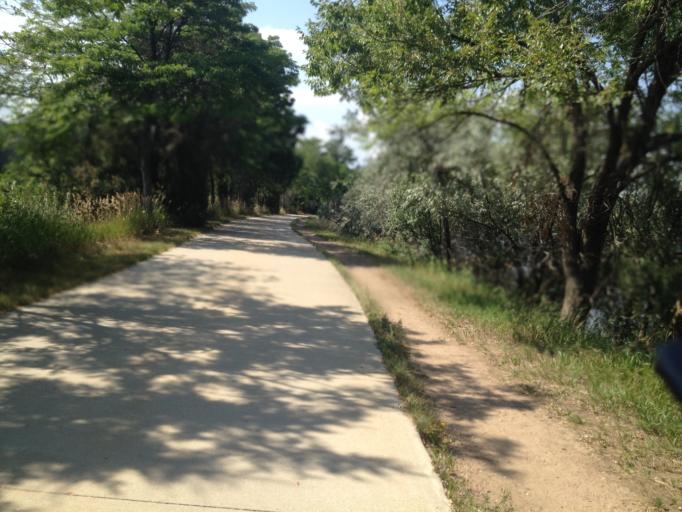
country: US
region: Colorado
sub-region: Boulder County
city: Boulder
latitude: 40.0257
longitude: -105.2175
